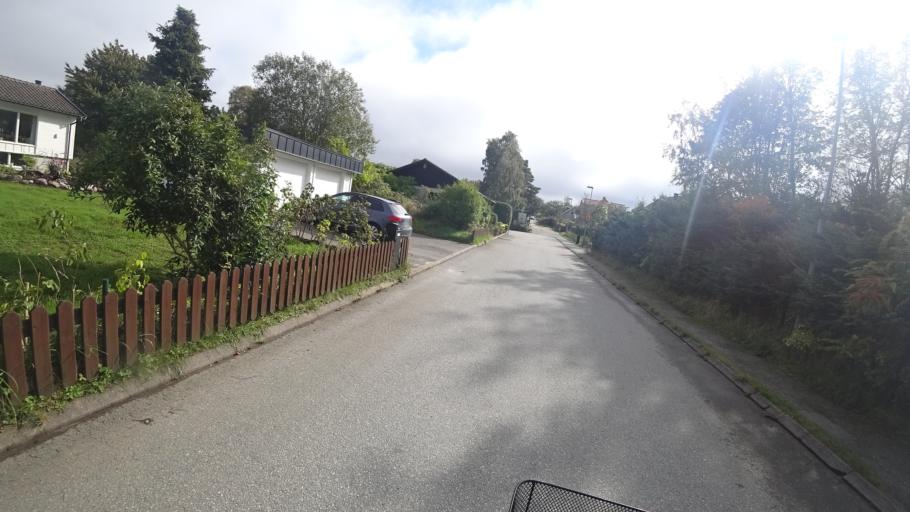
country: SE
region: Vaestra Goetaland
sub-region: Molndal
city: Moelndal
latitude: 57.6320
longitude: 11.9535
